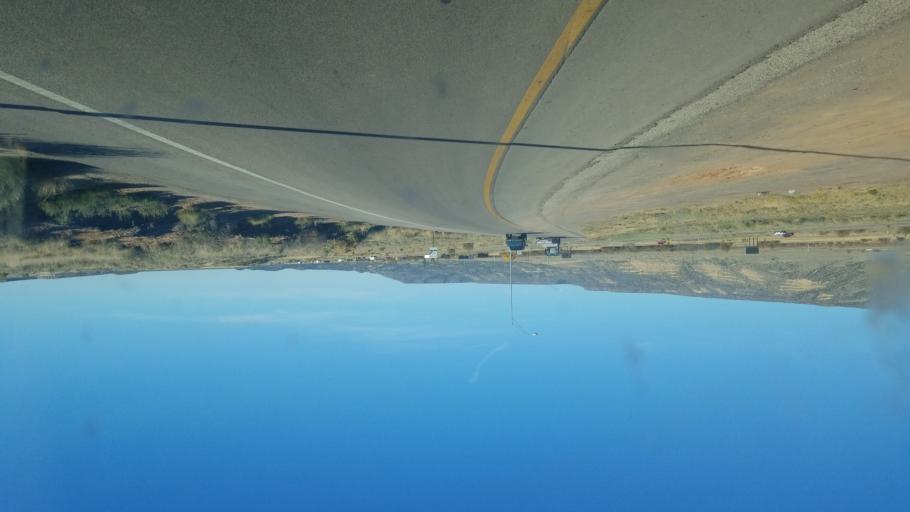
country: US
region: New Mexico
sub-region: Cibola County
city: Grants
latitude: 35.1221
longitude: -107.8305
